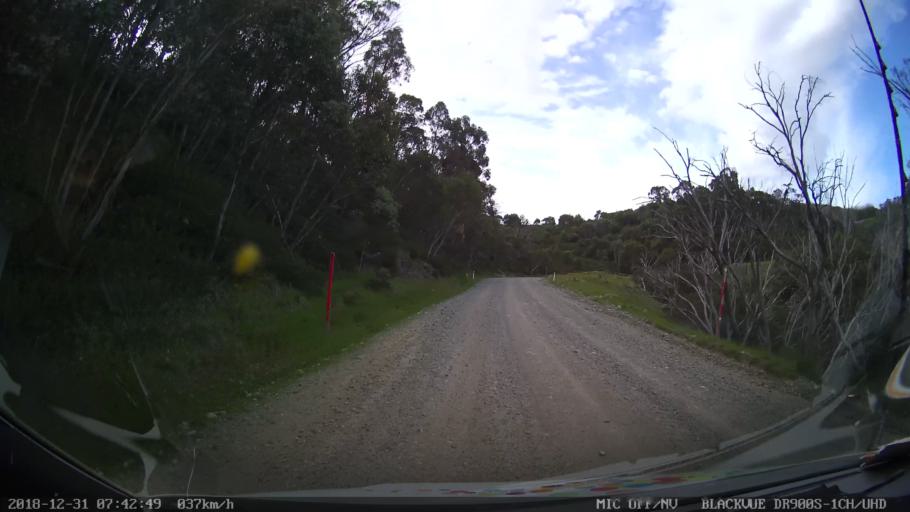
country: AU
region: New South Wales
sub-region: Snowy River
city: Jindabyne
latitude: -36.3583
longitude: 148.4079
